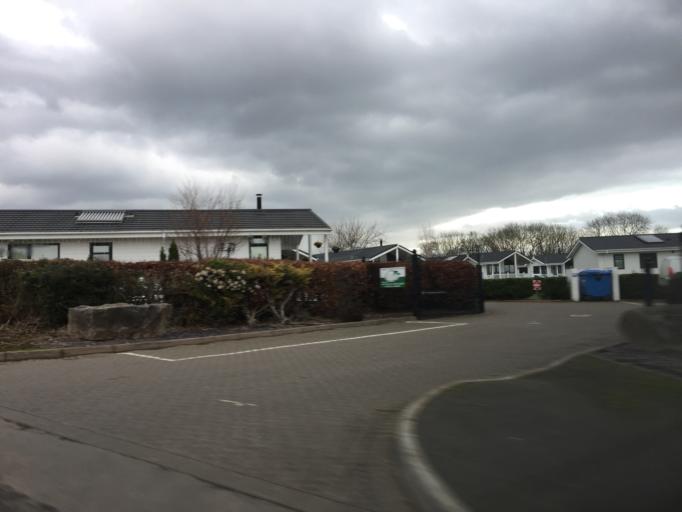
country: GB
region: Wales
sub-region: Monmouthshire
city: Chepstow
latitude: 51.6078
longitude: -2.7117
